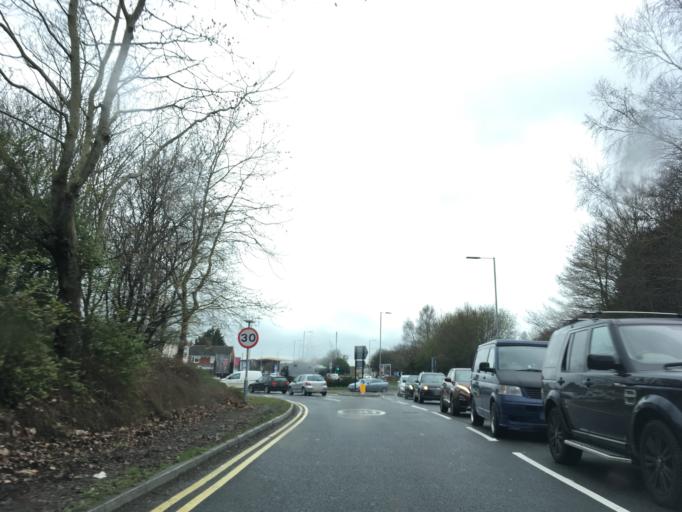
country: GB
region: England
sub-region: Borough of Swindon
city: Swindon
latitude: 51.5677
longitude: -1.8003
